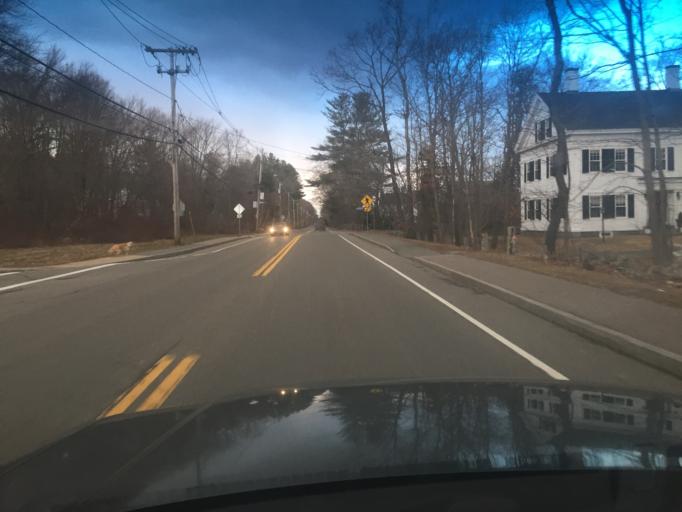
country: US
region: Massachusetts
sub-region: Middlesex County
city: Holliston
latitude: 42.1583
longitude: -71.4435
